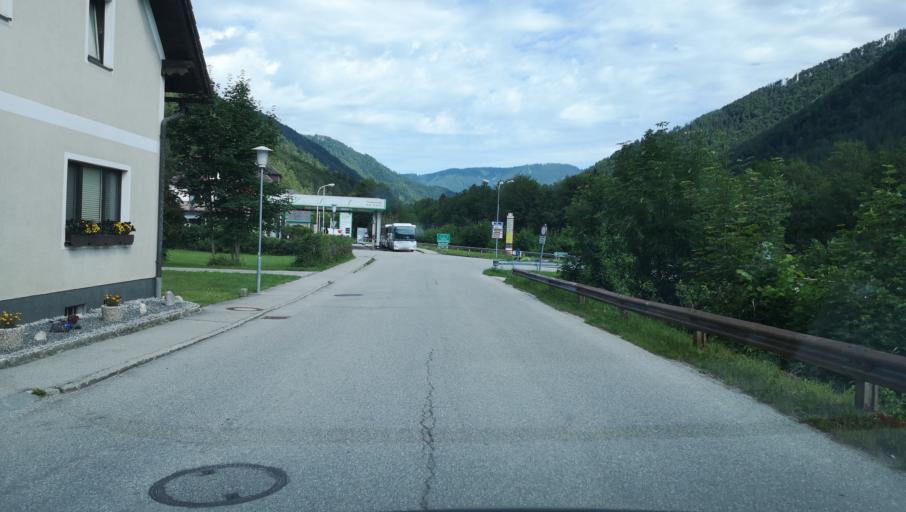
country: AT
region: Lower Austria
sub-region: Politischer Bezirk Amstetten
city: Hollenstein an der Ybbs
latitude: 47.8048
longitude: 14.7706
